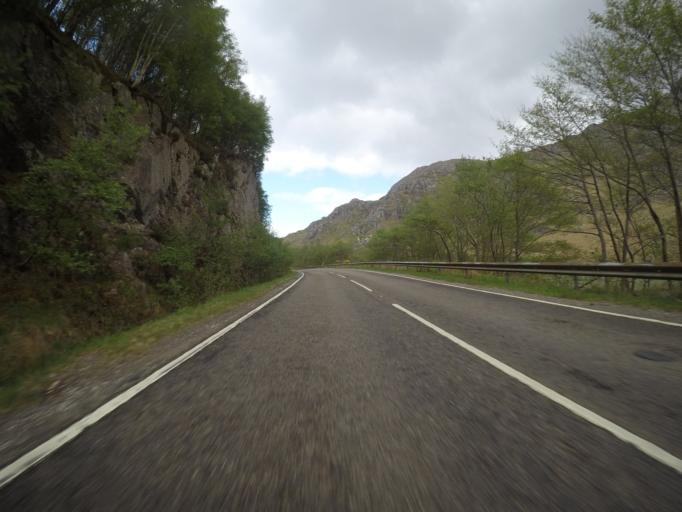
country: GB
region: Scotland
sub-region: Highland
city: Fort William
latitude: 57.2100
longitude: -5.4091
